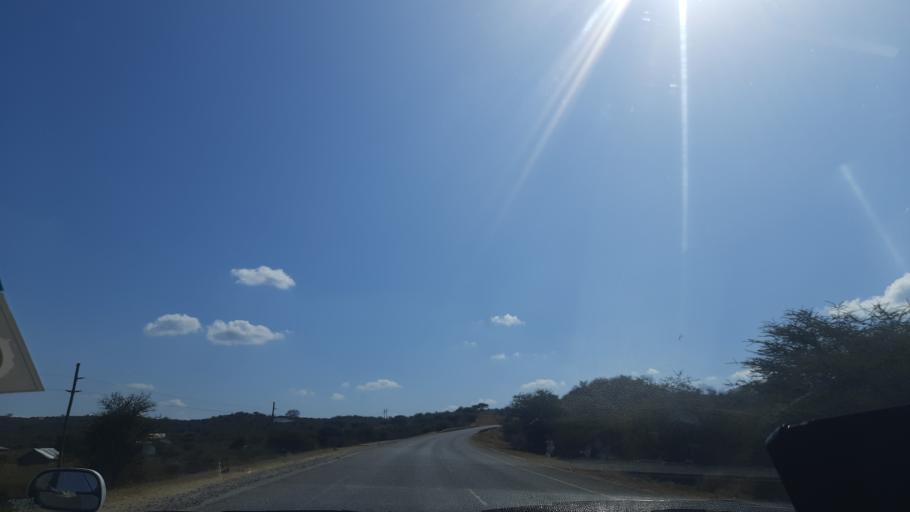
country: TZ
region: Singida
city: Kilimatinde
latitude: -5.7830
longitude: 34.8875
